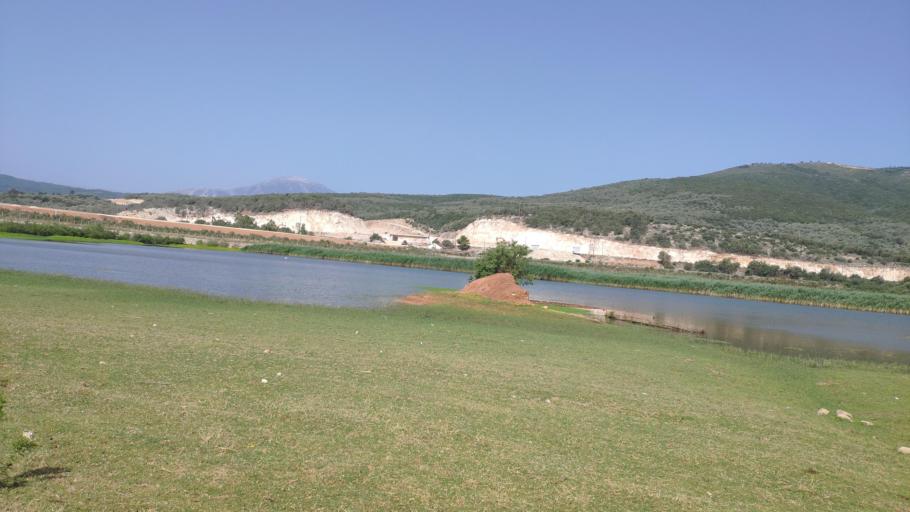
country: GR
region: West Greece
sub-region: Nomos Aitolias kai Akarnanias
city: Stanos
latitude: 38.7795
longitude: 21.1907
